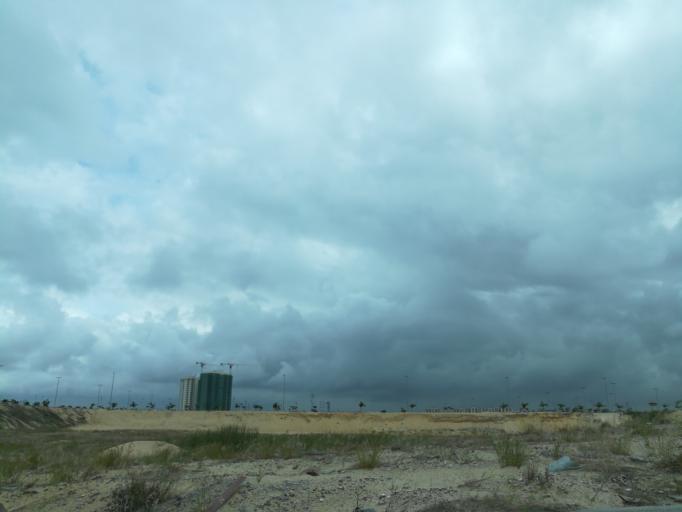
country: NG
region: Lagos
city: Ikoyi
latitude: 6.4132
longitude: 3.4150
